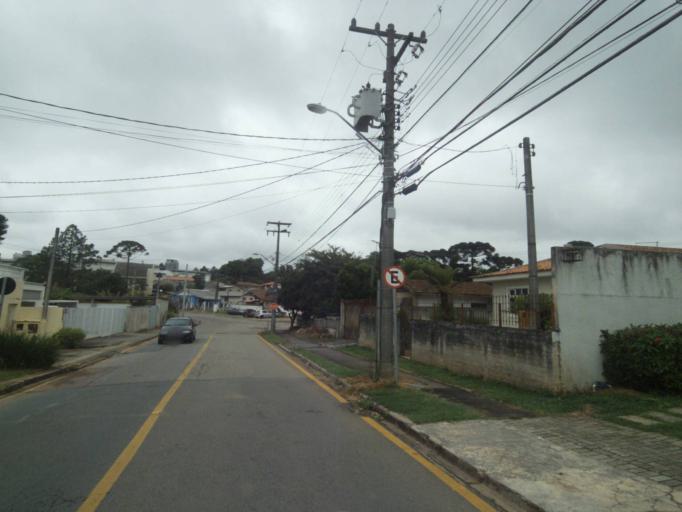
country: BR
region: Parana
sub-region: Curitiba
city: Curitiba
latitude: -25.4285
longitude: -49.3373
